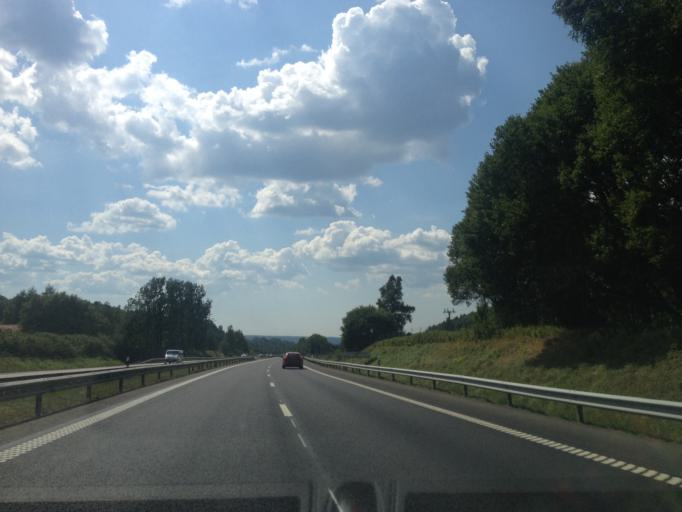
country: SE
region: Vaestra Goetaland
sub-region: Lerums Kommun
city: Stenkullen
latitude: 57.7891
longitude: 12.3319
